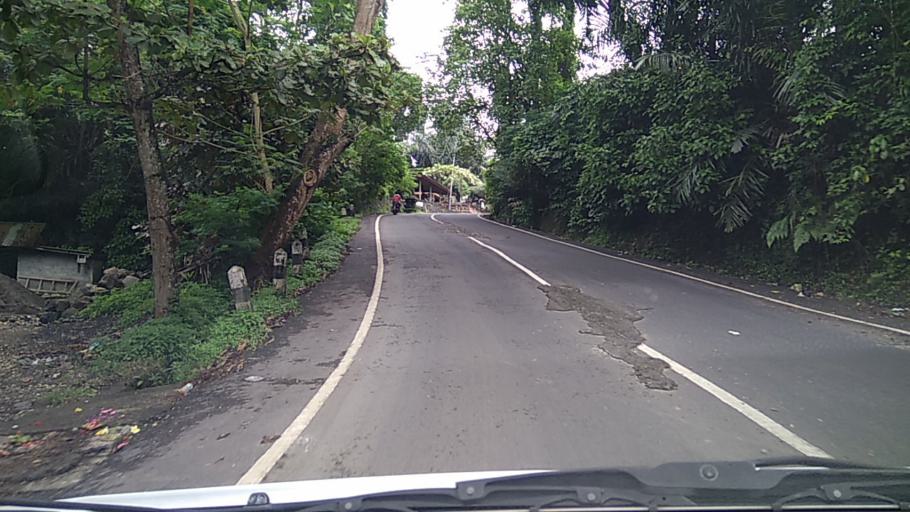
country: ID
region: Bali
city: Banjar Keraman
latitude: -8.5284
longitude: 115.2271
